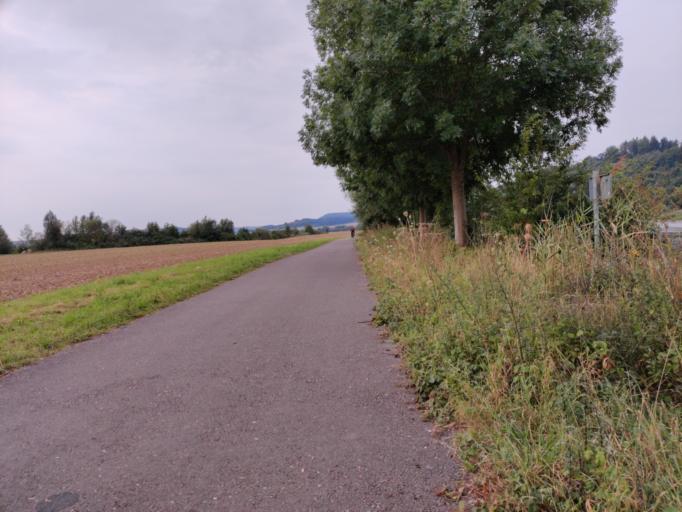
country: DE
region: Lower Saxony
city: Hameln
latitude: 52.0802
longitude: 9.3678
